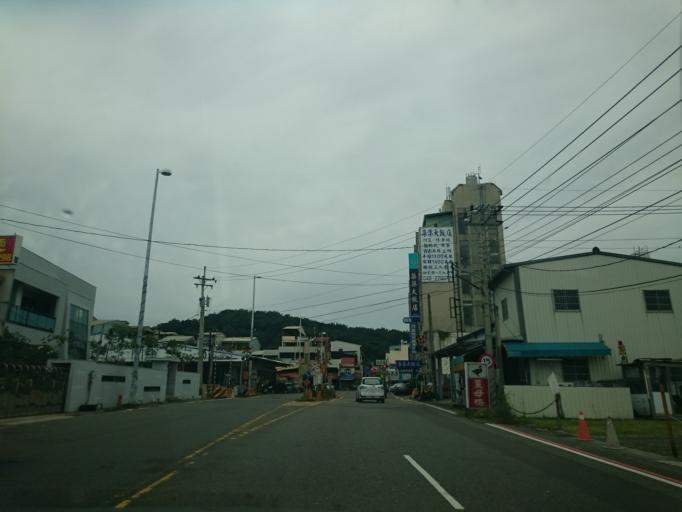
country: TW
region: Taiwan
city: Lugu
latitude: 23.8258
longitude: 120.7837
